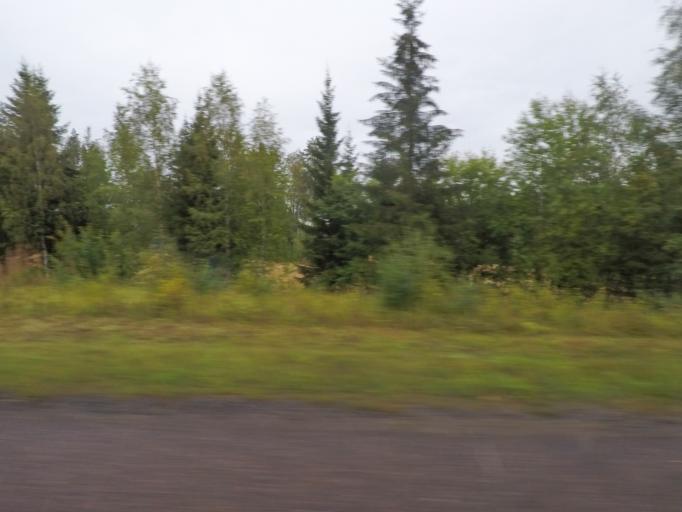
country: FI
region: Northern Savo
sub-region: Varkaus
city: Leppaevirta
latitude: 62.4456
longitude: 27.7971
